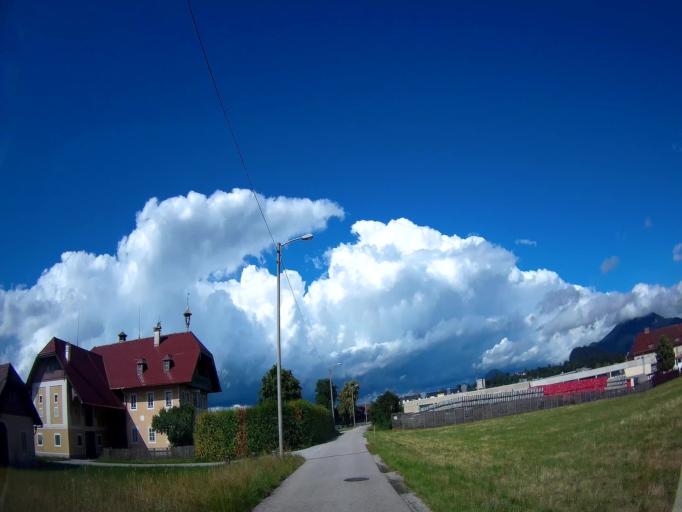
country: AT
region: Salzburg
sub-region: Salzburg Stadt
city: Salzburg
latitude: 47.7965
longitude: 13.0156
